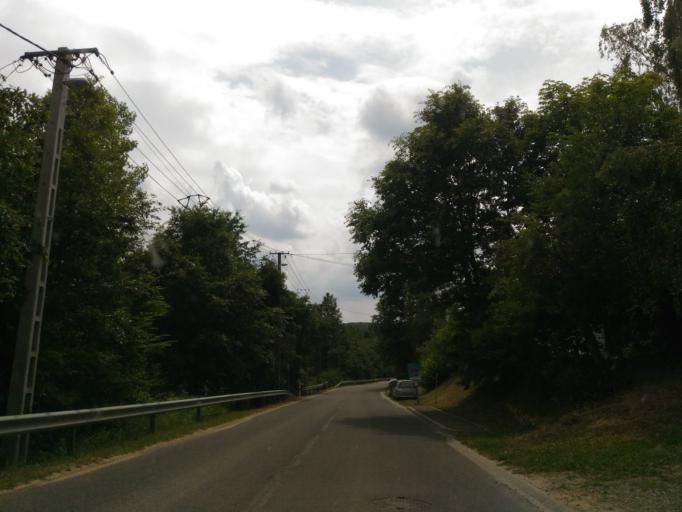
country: HU
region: Baranya
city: Komlo
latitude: 46.1776
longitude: 18.2306
